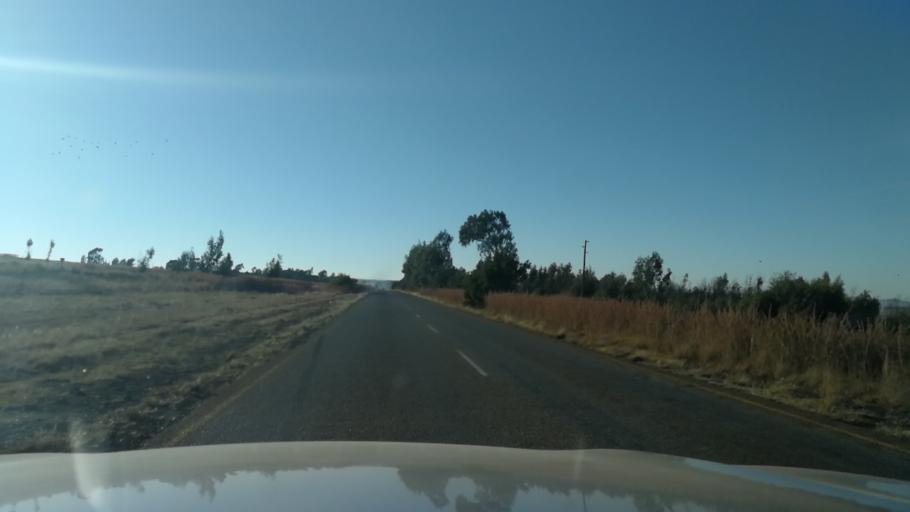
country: ZA
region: North-West
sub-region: Bojanala Platinum District Municipality
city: Koster
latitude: -25.9190
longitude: 27.0830
